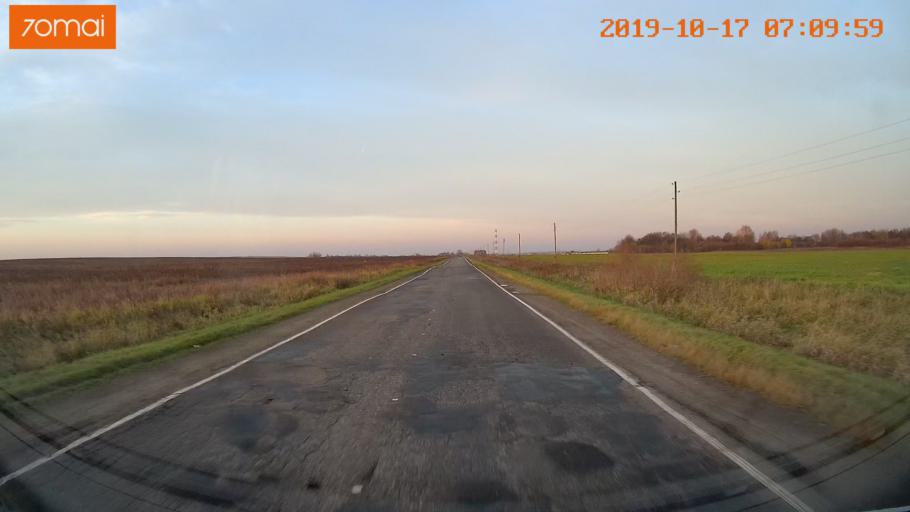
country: RU
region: Vladimir
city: Suzdal'
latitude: 56.4149
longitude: 40.3713
